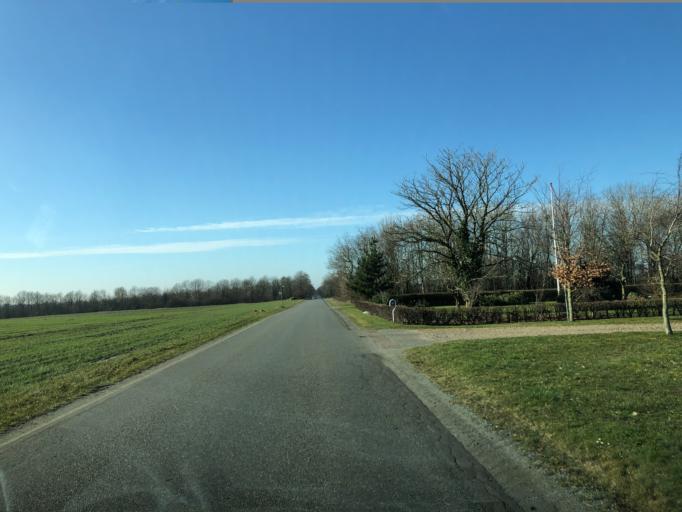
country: DK
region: Central Jutland
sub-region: Ikast-Brande Kommune
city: Bording Kirkeby
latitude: 56.1530
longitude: 9.2970
